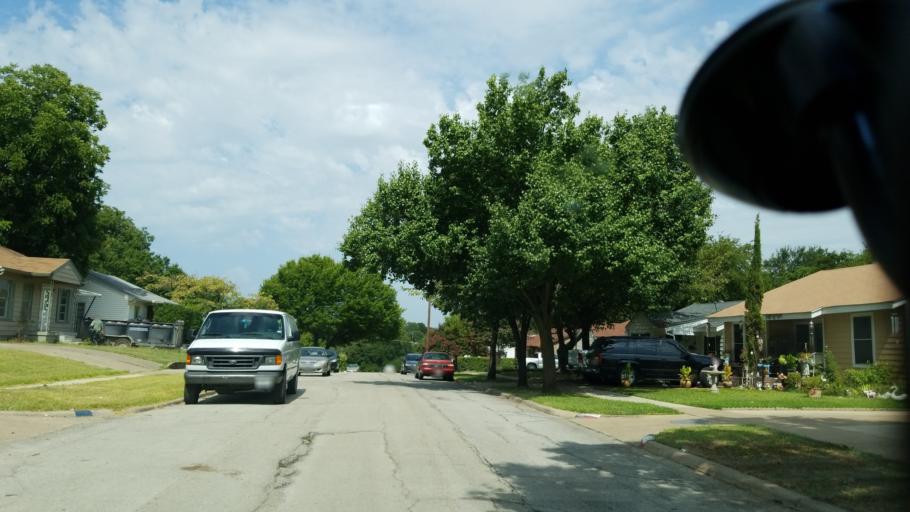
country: US
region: Texas
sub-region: Dallas County
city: Grand Prairie
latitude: 32.7517
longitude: -96.9927
